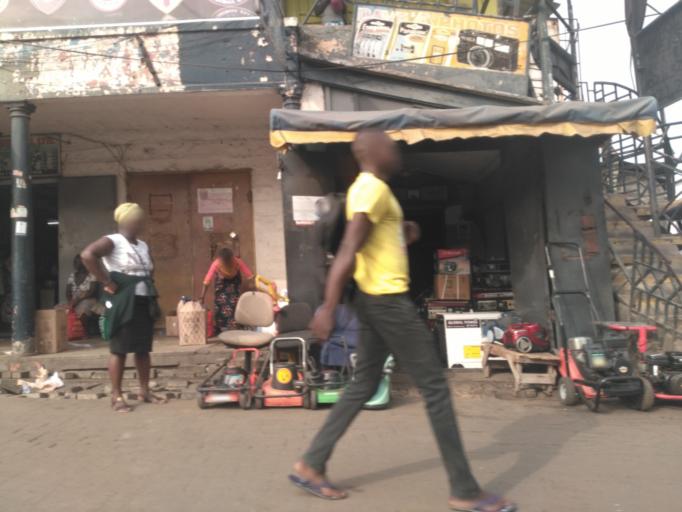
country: GH
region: Greater Accra
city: Accra
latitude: 5.5437
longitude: -0.2095
